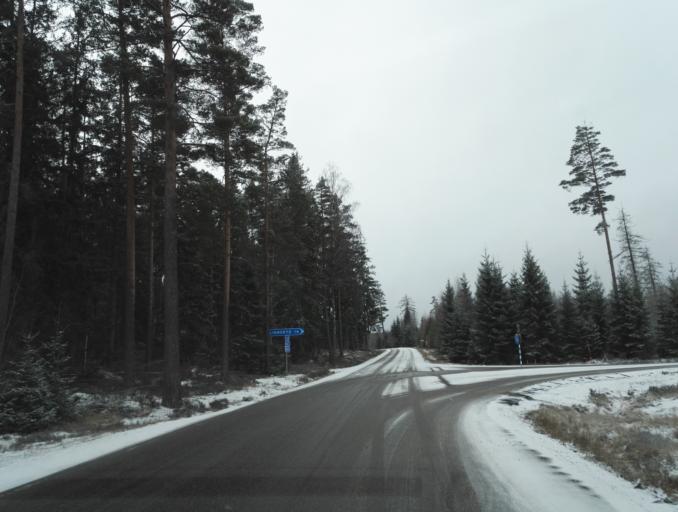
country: SE
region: Kronoberg
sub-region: Lessebo Kommun
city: Lessebo
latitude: 56.7399
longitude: 15.2619
